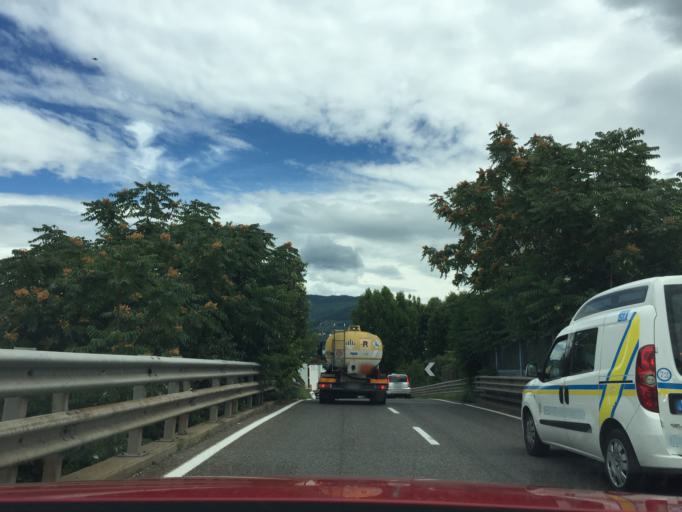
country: IT
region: Tuscany
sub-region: Province of Florence
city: Sesto Fiorentino
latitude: 43.7977
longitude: 11.2039
